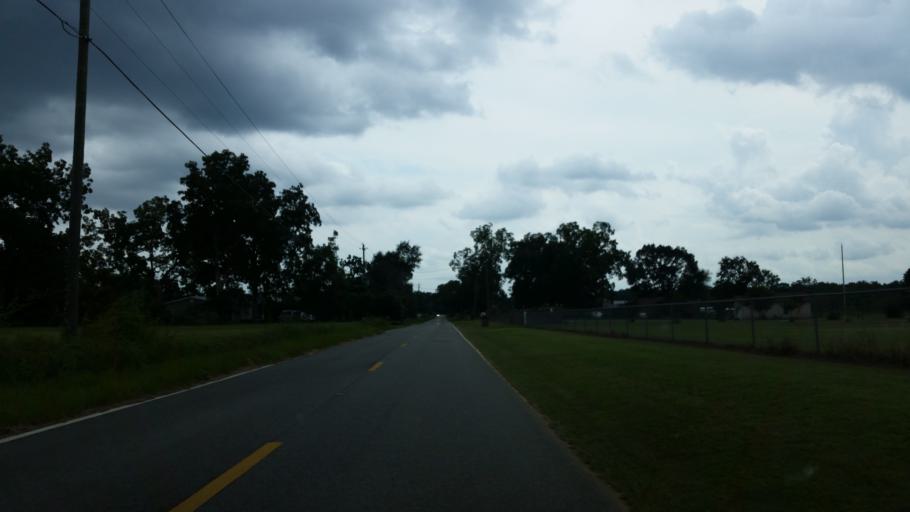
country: US
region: Florida
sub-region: Escambia County
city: Molino
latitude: 30.6979
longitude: -87.4054
